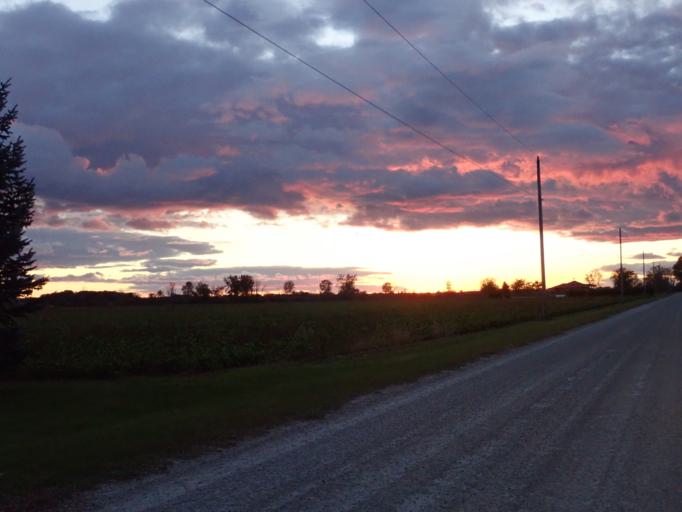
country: CA
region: Ontario
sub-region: Lambton County
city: Walpole Island
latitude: 42.6055
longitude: -82.4066
